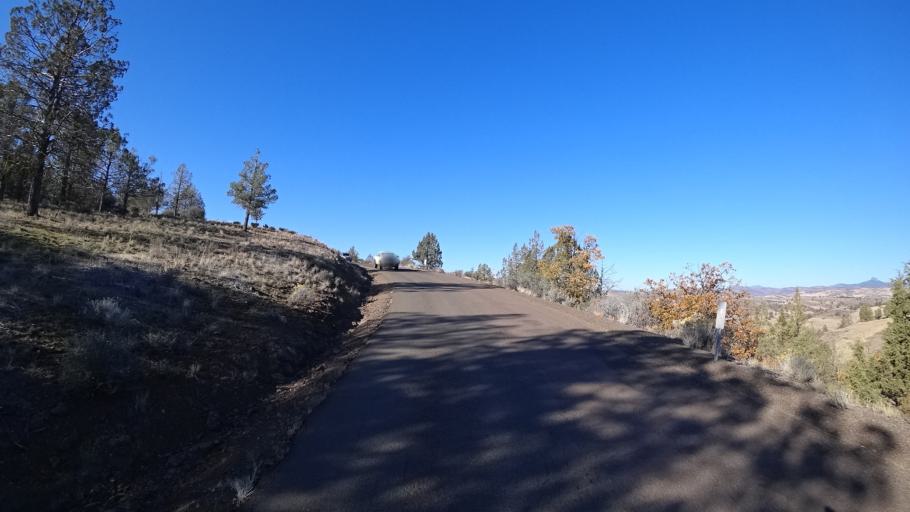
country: US
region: California
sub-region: Siskiyou County
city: Montague
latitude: 41.9112
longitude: -122.4358
